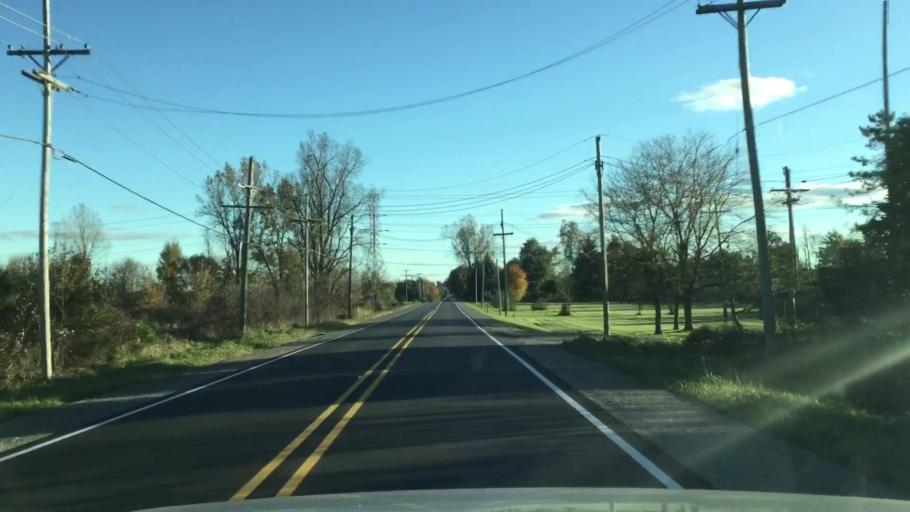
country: US
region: Michigan
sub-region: Lapeer County
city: Almont
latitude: 42.9402
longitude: -83.1446
